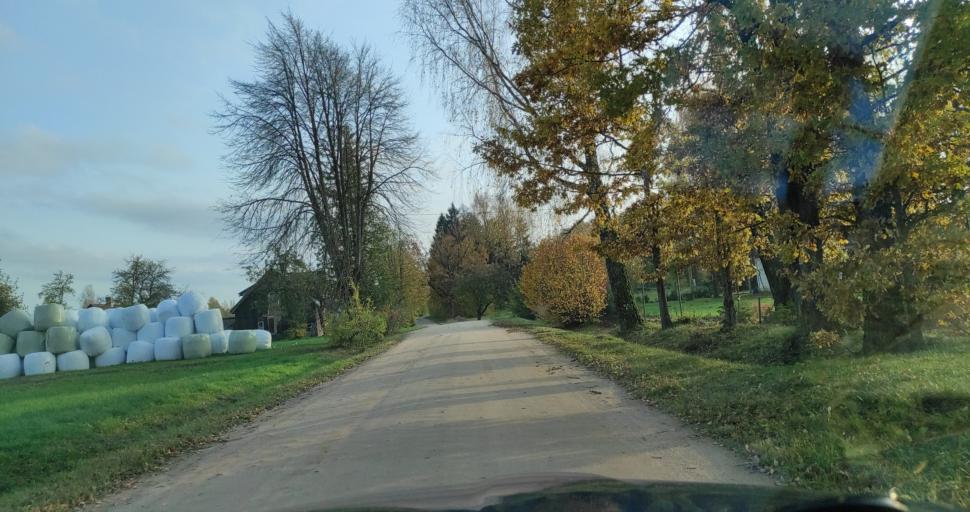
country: LV
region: Vainode
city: Vainode
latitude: 56.4252
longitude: 21.8737
